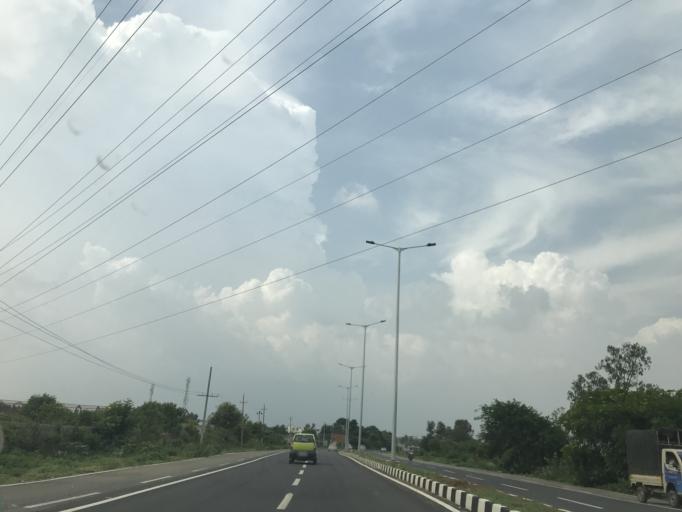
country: IN
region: Karnataka
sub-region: Bangalore Rural
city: Devanhalli
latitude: 13.1662
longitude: 77.6875
